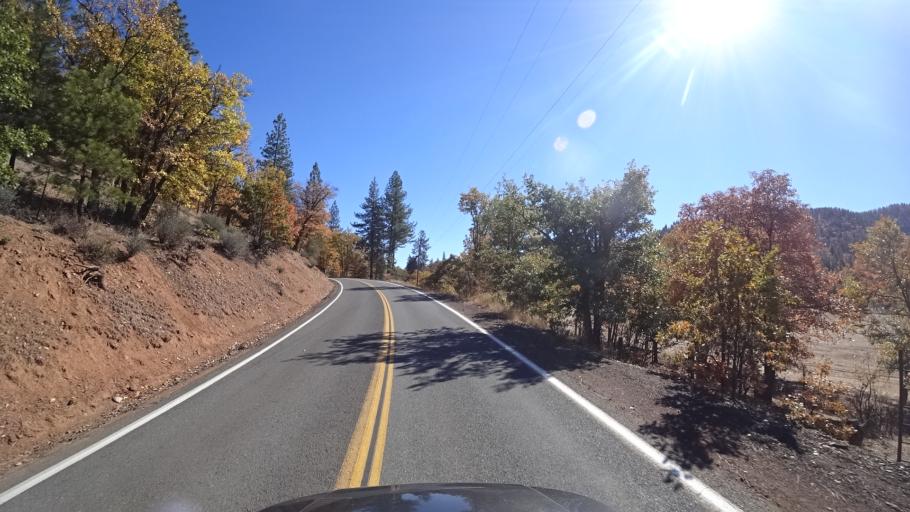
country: US
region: California
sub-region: Siskiyou County
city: Yreka
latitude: 41.5699
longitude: -122.9420
